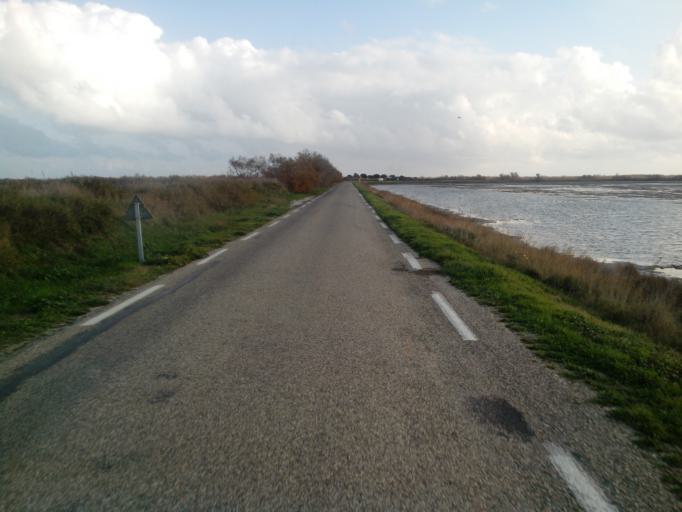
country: FR
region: Provence-Alpes-Cote d'Azur
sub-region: Departement des Bouches-du-Rhone
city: Port-Saint-Louis-du-Rhone
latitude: 43.3750
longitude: 4.8042
